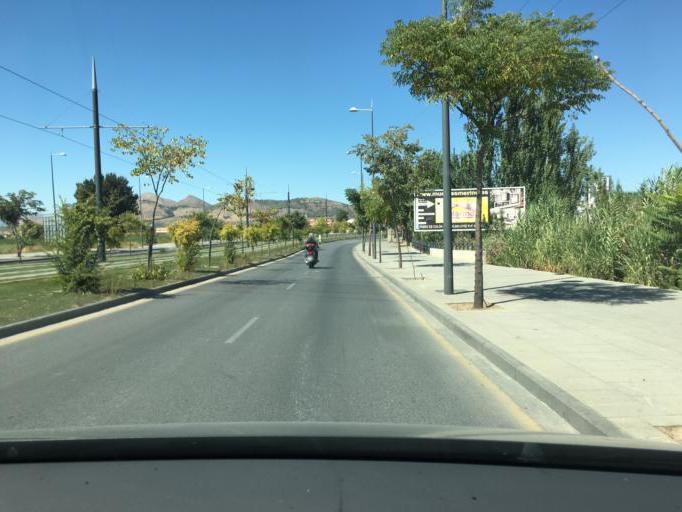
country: ES
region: Andalusia
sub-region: Provincia de Granada
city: Maracena
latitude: 37.2183
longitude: -3.6422
